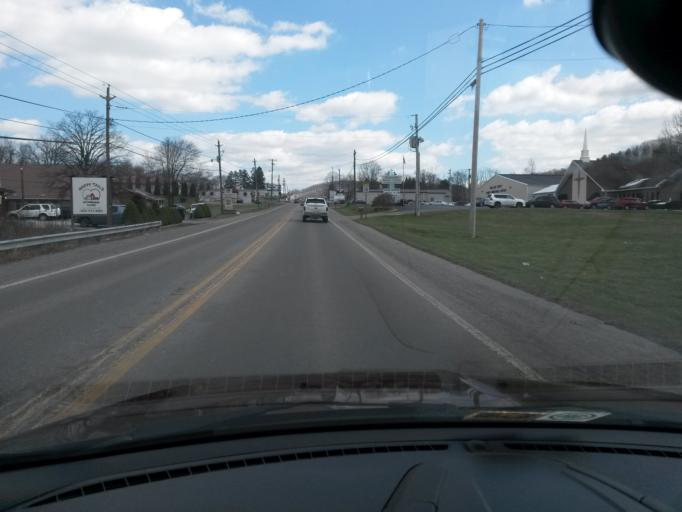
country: US
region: West Virginia
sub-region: Mercer County
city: Princeton
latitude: 37.3651
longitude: -81.0688
